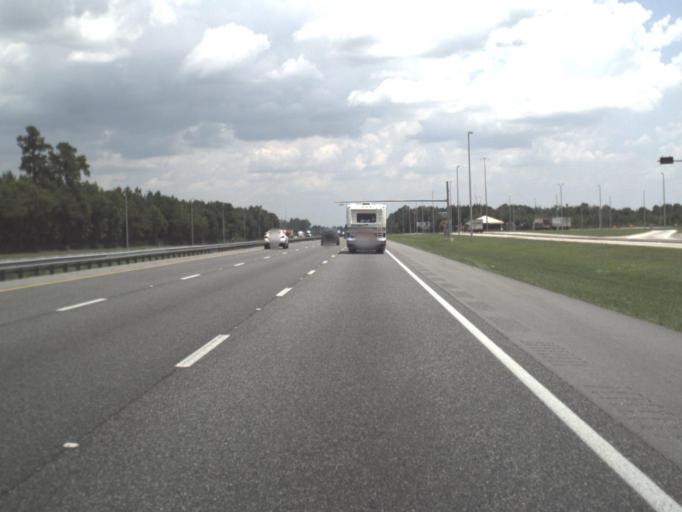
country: US
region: Florida
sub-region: Hamilton County
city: Jasper
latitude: 30.4247
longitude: -82.9049
